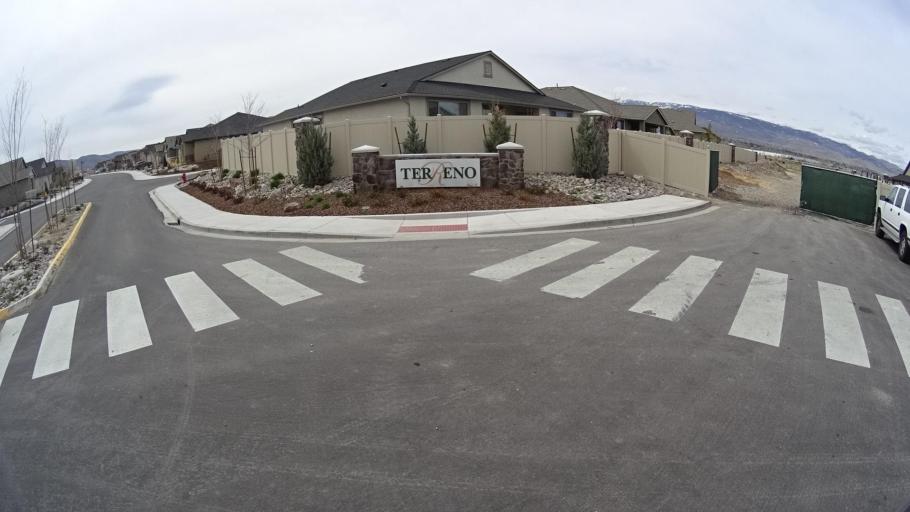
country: US
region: Nevada
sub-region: Washoe County
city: Sparks
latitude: 39.4167
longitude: -119.7345
